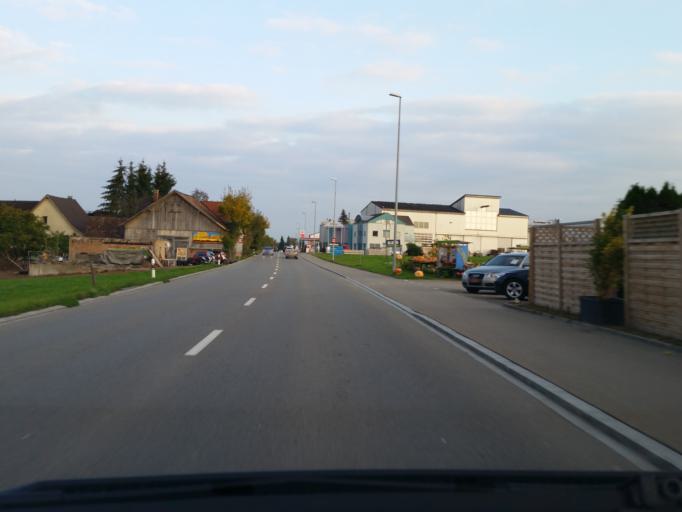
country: CH
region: Thurgau
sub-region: Arbon District
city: Uttwil
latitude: 47.5757
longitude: 9.3576
